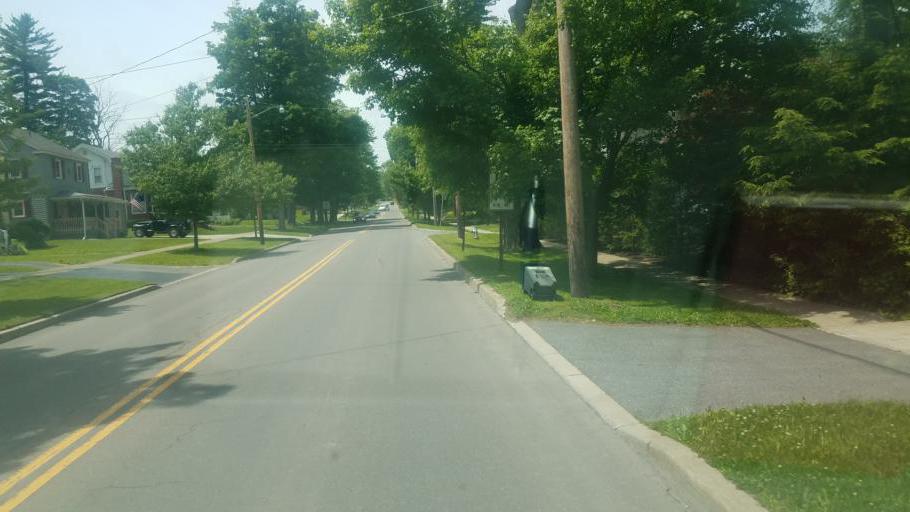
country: US
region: Pennsylvania
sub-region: Tioga County
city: Wellsboro
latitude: 41.7439
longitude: -77.3101
